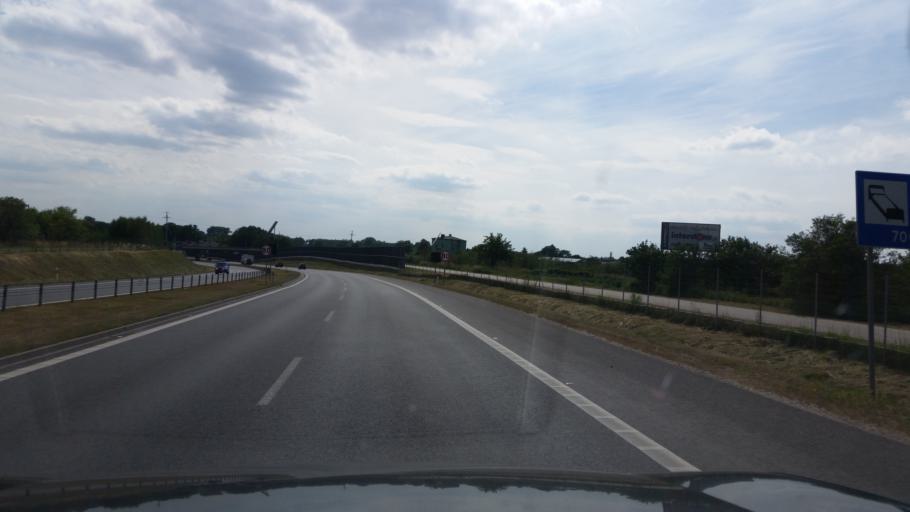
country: PL
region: Masovian Voivodeship
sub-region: Powiat zyrardowski
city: Mszczonow
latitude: 51.9794
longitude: 20.5102
